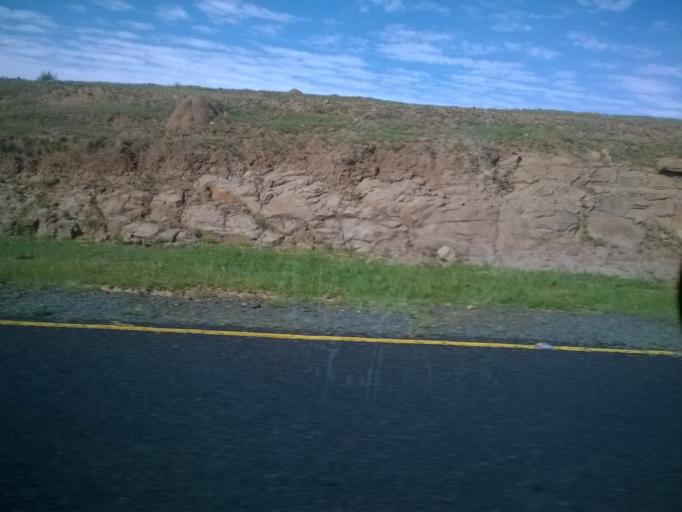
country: LS
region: Berea
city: Teyateyaneng
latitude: -29.0813
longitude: 27.8772
